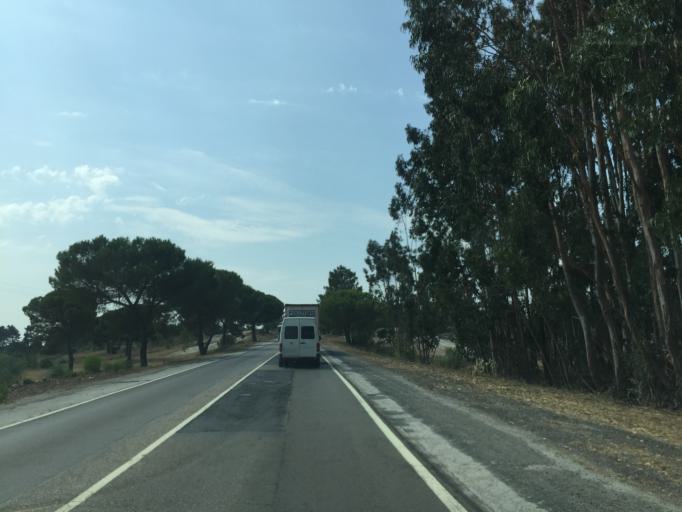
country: PT
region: Setubal
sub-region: Alcacer do Sal
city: Alcacer do Sal
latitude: 38.2932
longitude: -8.5347
